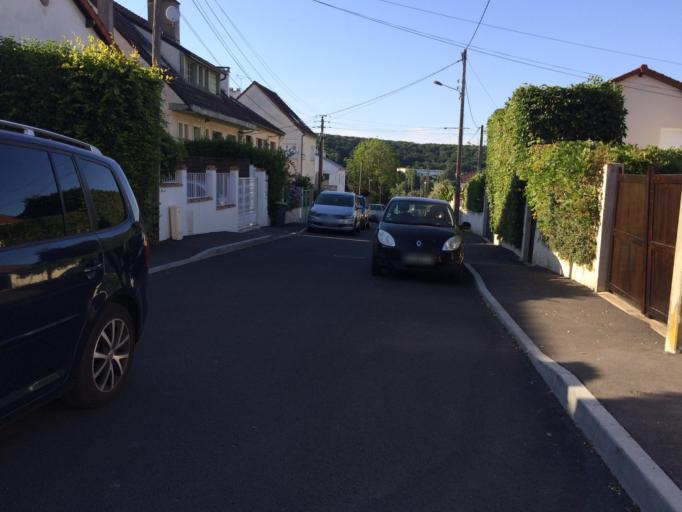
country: FR
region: Ile-de-France
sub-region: Departement de l'Essonne
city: Igny
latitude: 48.7310
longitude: 2.2191
